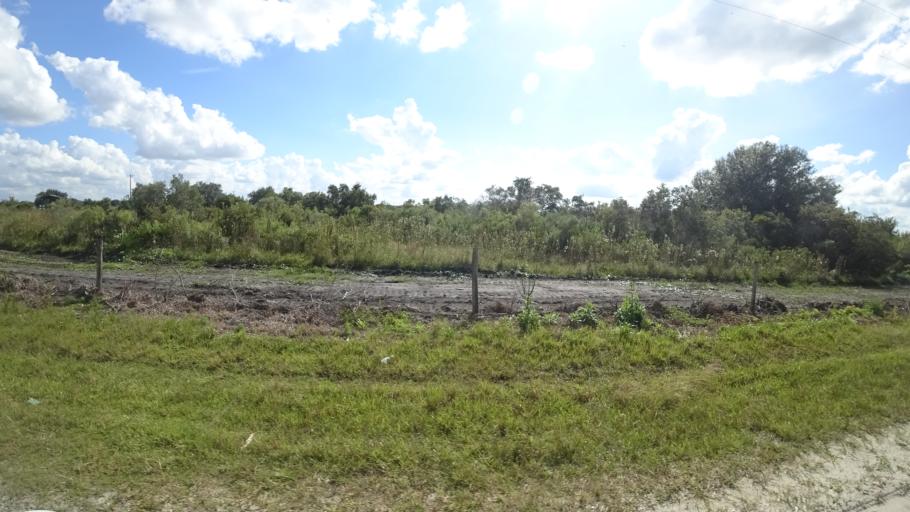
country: US
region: Florida
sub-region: Sarasota County
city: Lake Sarasota
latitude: 27.4219
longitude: -82.1341
